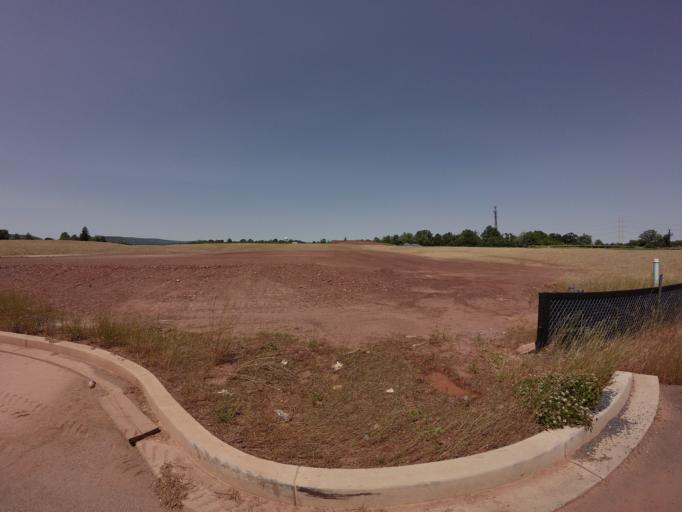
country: US
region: Maryland
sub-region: Frederick County
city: Ballenger Creek
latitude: 39.3954
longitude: -77.4529
